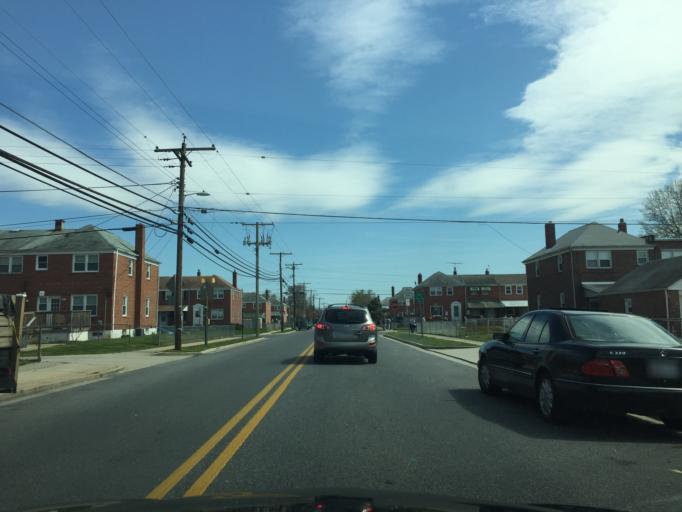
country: US
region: Maryland
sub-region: Baltimore County
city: Middle River
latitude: 39.3249
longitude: -76.4368
